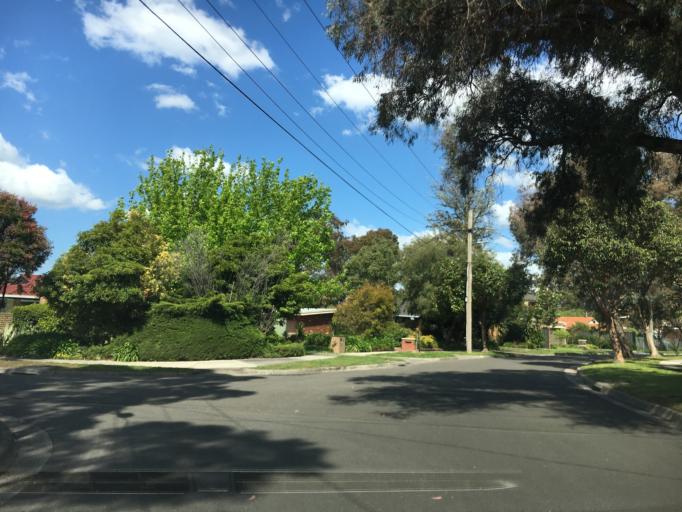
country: AU
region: Victoria
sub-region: Knox
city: Wantirna South
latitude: -37.8883
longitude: 145.1903
